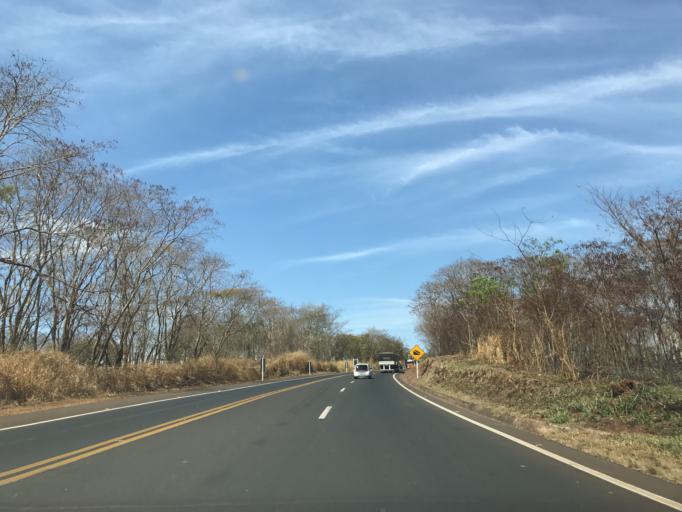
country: BR
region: Minas Gerais
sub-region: Monte Alegre De Minas
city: Monte Alegre de Minas
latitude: -18.9473
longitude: -49.0256
